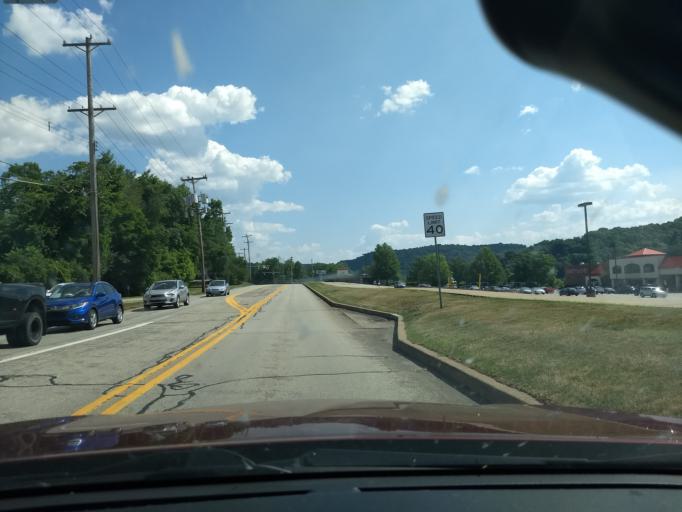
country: US
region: Pennsylvania
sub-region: Westmoreland County
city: Trafford
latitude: 40.3905
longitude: -79.7660
